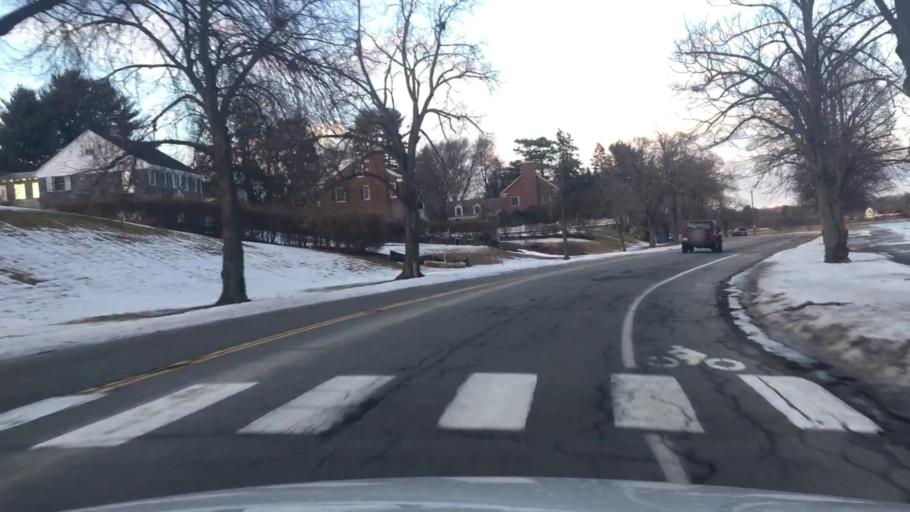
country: US
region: Maine
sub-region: Cumberland County
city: Portland
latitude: 43.6733
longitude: -70.2774
